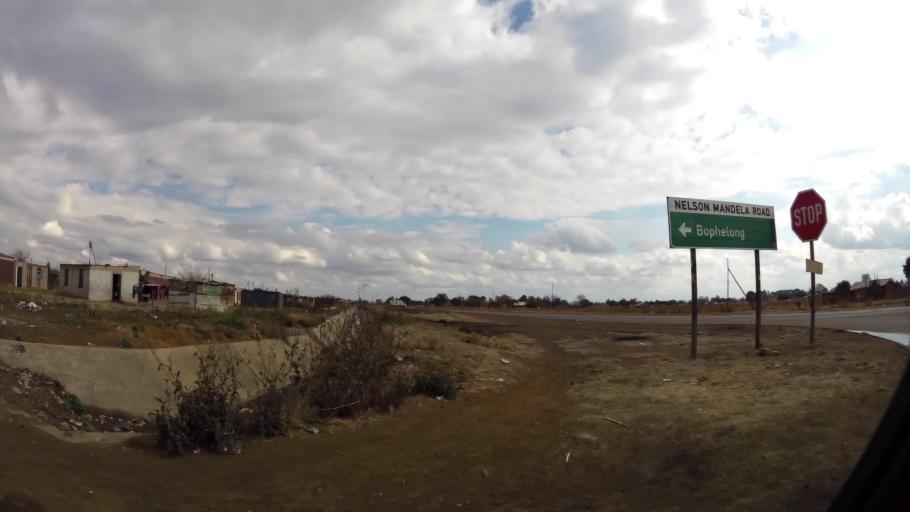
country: ZA
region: Gauteng
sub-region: Sedibeng District Municipality
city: Vanderbijlpark
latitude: -26.6796
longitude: 27.7806
